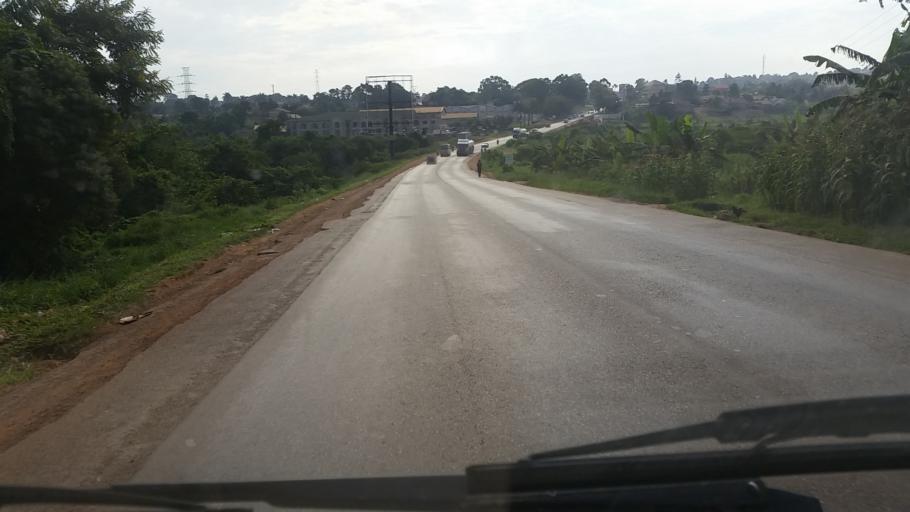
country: UG
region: Central Region
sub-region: Wakiso District
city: Bweyogerere
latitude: 0.3659
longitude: 32.7033
